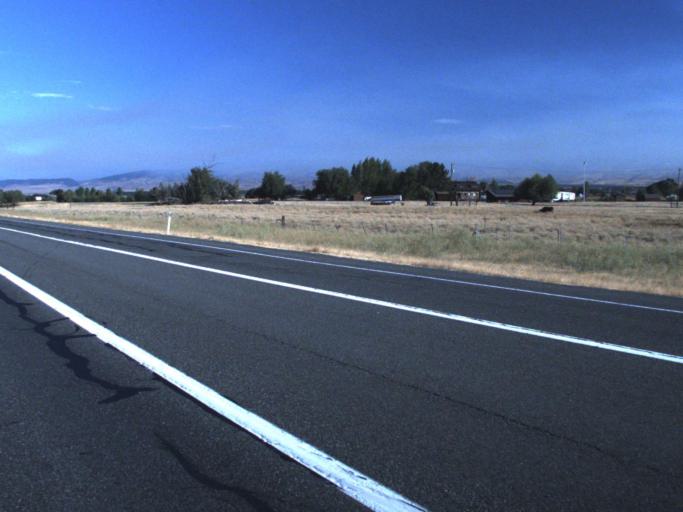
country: US
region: Washington
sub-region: Kittitas County
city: Ellensburg
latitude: 46.9307
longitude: -120.5018
